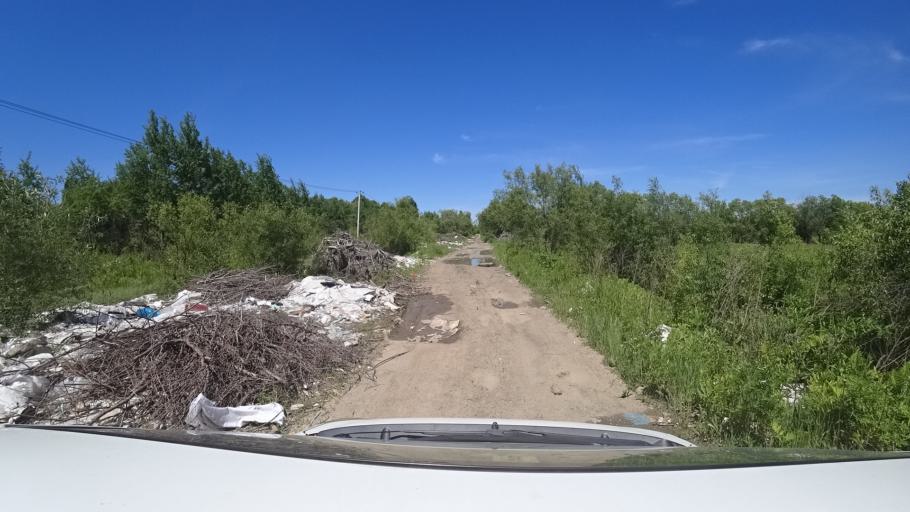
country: RU
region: Khabarovsk Krai
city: Topolevo
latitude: 48.4859
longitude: 135.1764
